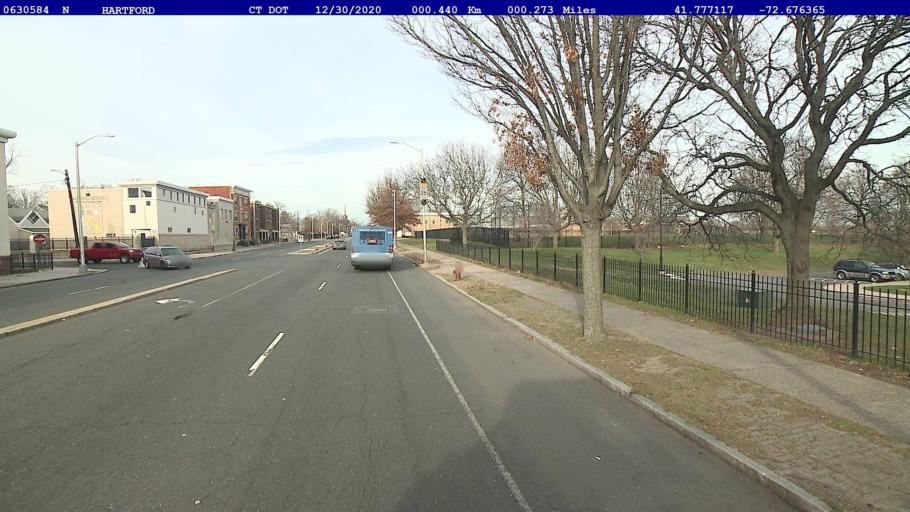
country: US
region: Connecticut
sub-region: Hartford County
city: Hartford
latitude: 41.7771
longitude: -72.6764
